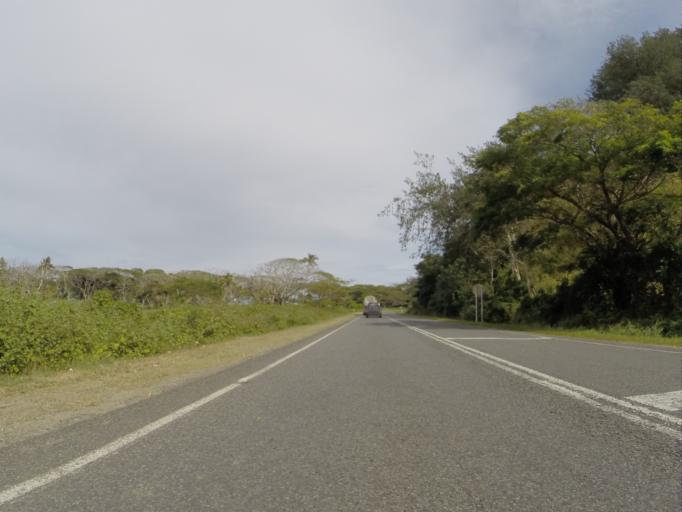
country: FJ
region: Western
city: Nadi
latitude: -18.1840
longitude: 177.5997
